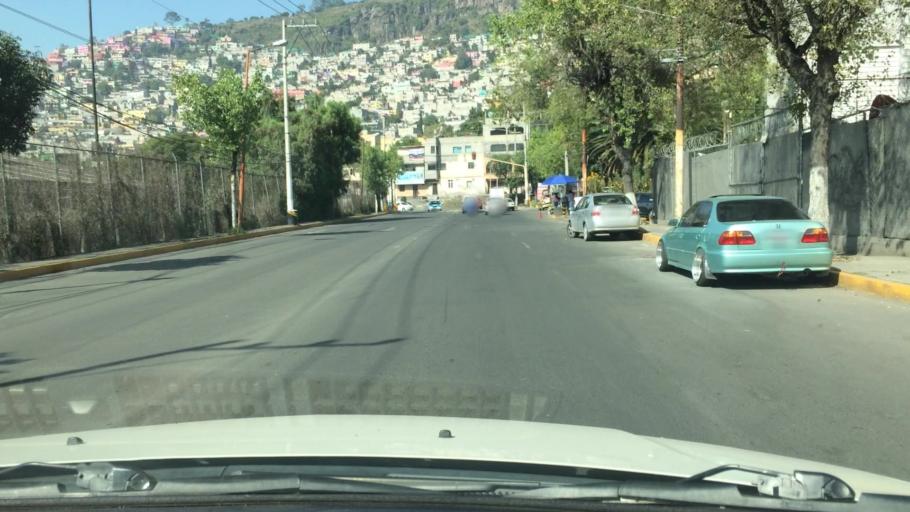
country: MX
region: Mexico
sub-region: Tlalnepantla de Baz
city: Puerto Escondido (Tepeolulco Puerto Escondido)
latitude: 19.5274
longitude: -99.1191
